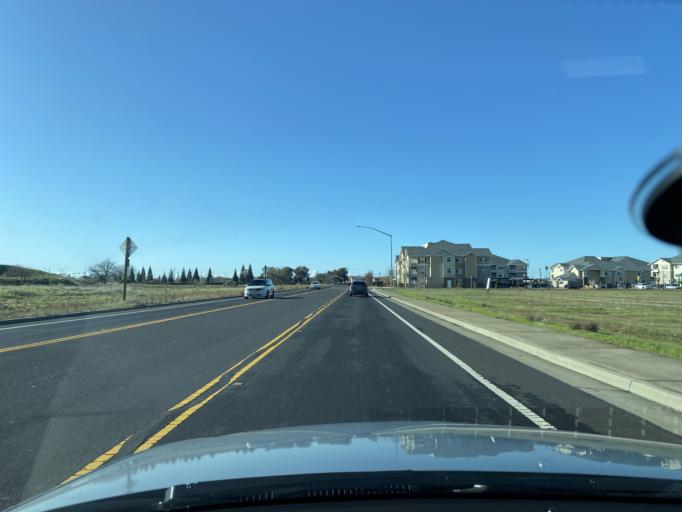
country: US
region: California
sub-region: Sacramento County
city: Laguna
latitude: 38.4399
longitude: -121.3979
